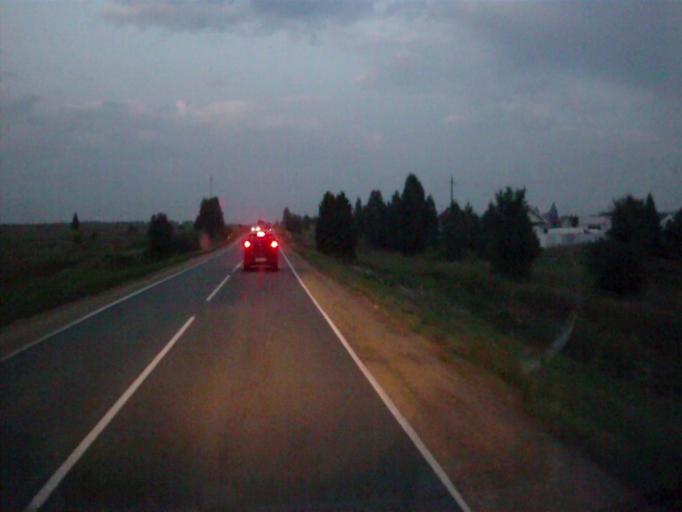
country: RU
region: Chelyabinsk
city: Poletayevo
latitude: 55.2105
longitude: 60.9039
